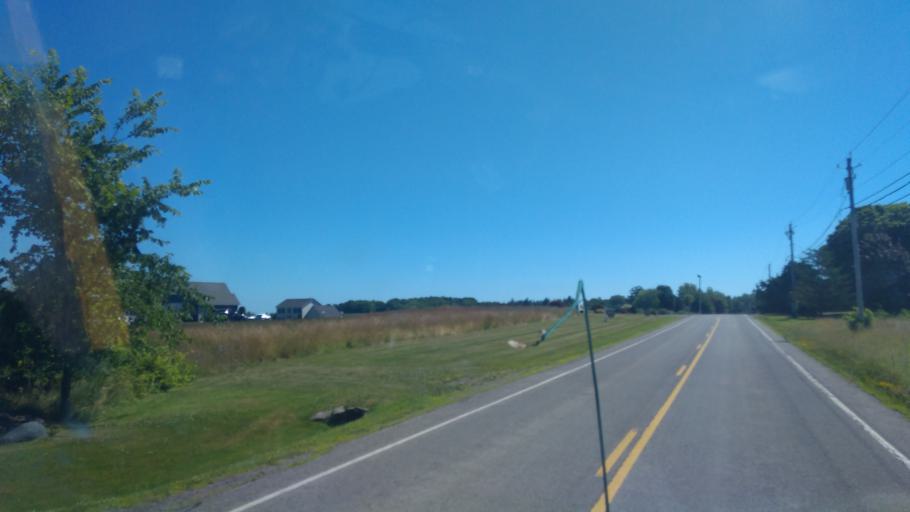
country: US
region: New York
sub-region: Wayne County
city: Williamson
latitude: 43.2821
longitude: -77.1571
